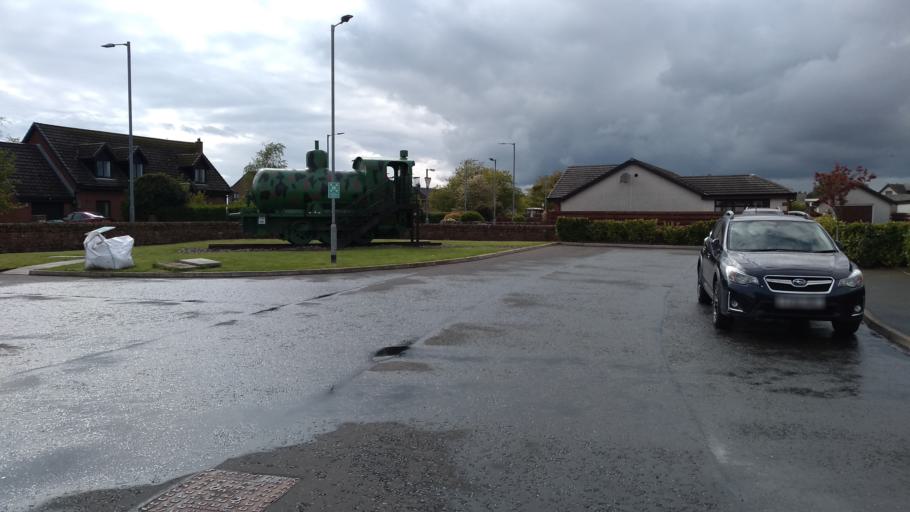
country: GB
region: Scotland
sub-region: Dumfries and Galloway
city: Annan
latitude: 54.9854
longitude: -3.1700
